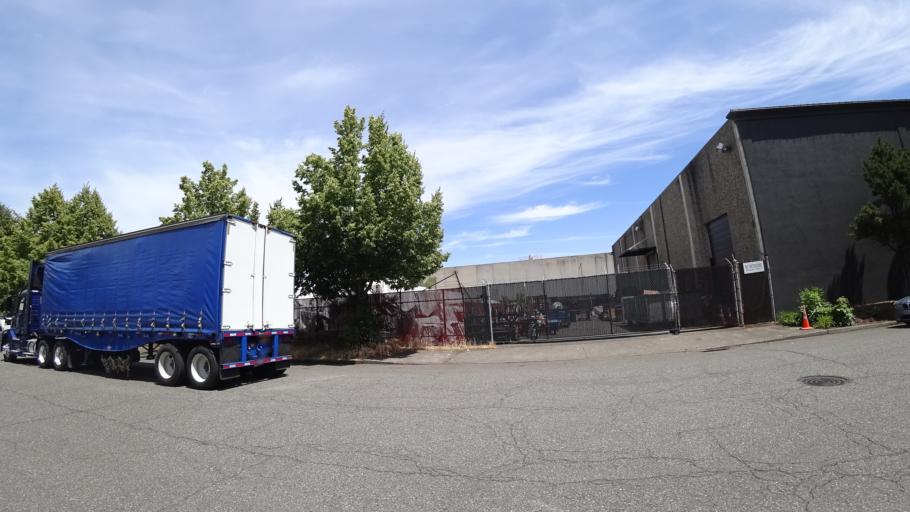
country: US
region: Oregon
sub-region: Multnomah County
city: Portland
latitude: 45.5391
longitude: -122.7140
